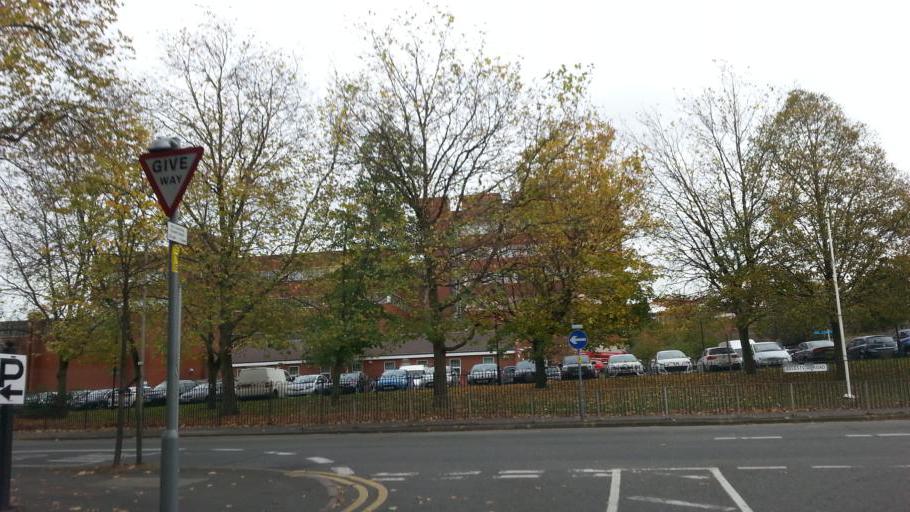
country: GB
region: England
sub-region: City of Leicester
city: Leicester
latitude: 52.6225
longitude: -1.1355
